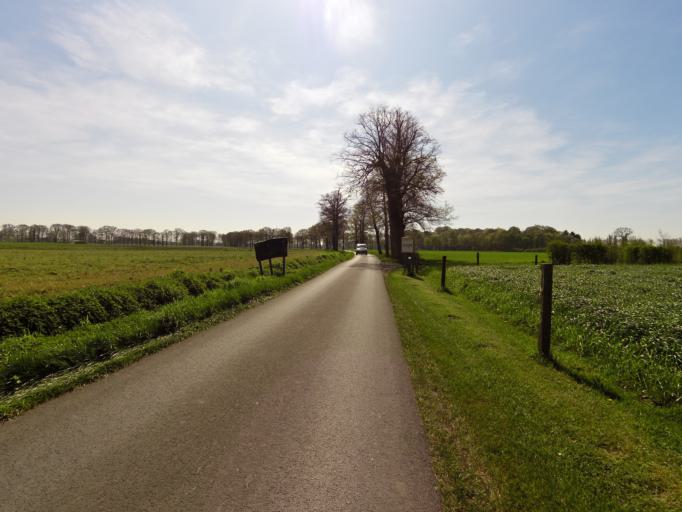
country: BE
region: Flanders
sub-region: Provincie West-Vlaanderen
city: Ichtegem
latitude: 51.1147
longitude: 3.0029
